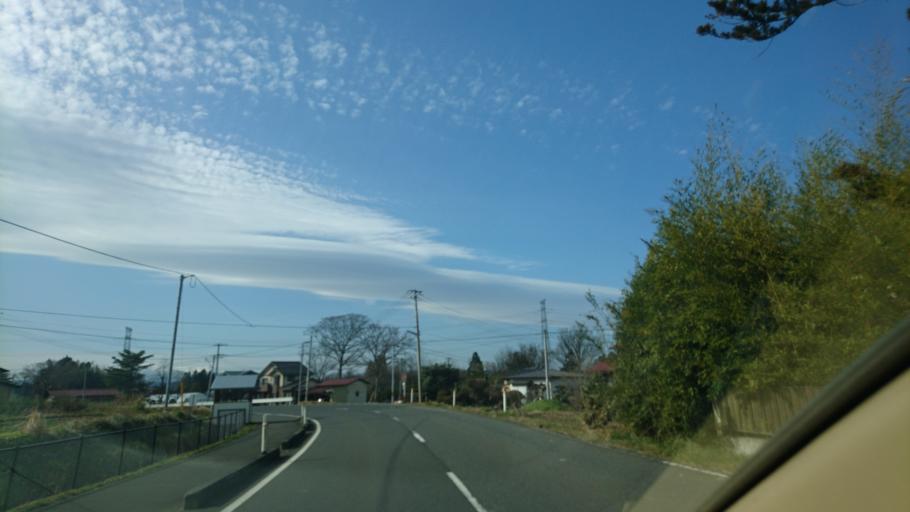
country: JP
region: Iwate
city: Ichinoseki
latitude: 38.8099
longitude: 141.0306
